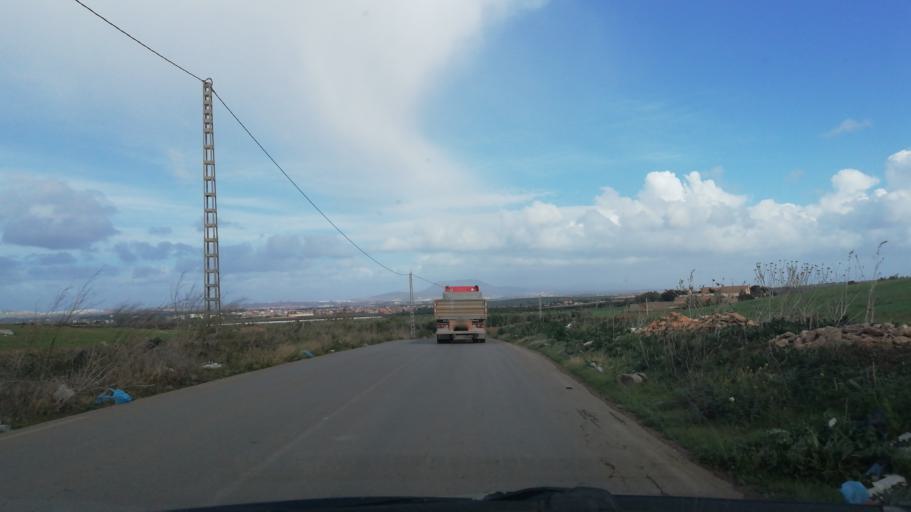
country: DZ
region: Oran
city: Sidi ech Chahmi
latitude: 35.6385
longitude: -0.5192
